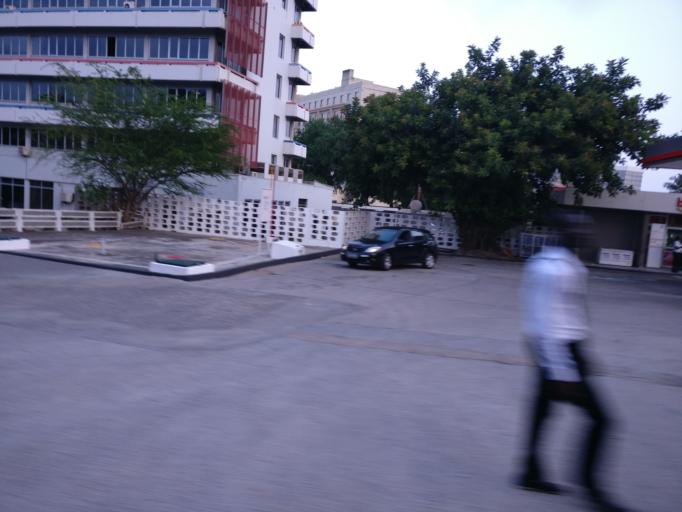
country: GH
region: Greater Accra
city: Accra
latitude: 5.5562
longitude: -0.2036
